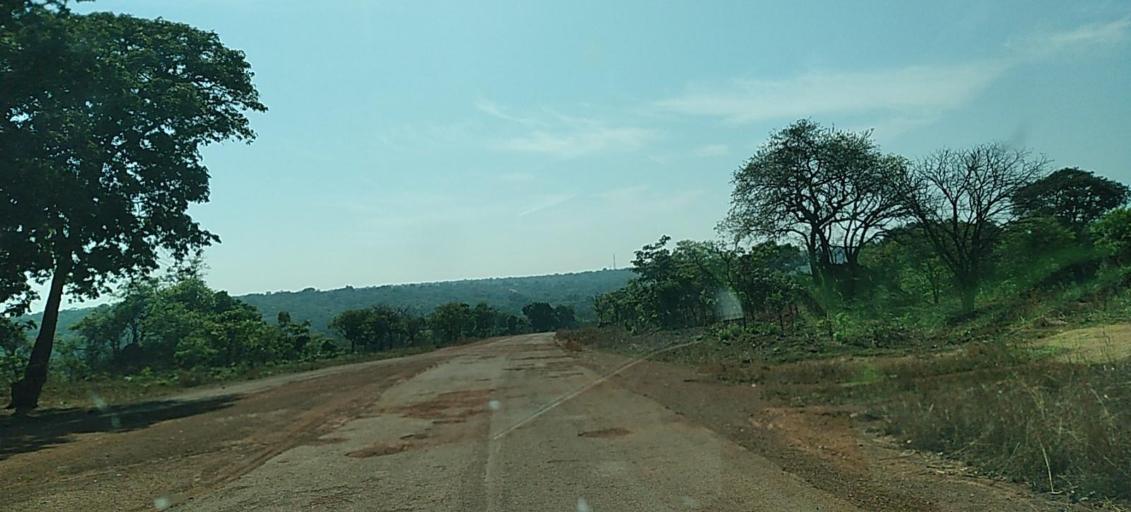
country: ZM
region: North-Western
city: Mwinilunga
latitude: -11.8234
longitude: 25.1189
